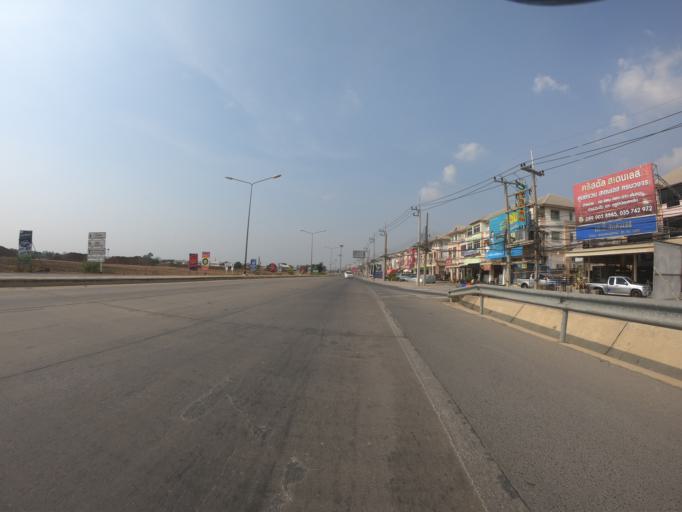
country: TH
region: Phra Nakhon Si Ayutthaya
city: Phra Nakhon Si Ayutthaya
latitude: 14.3336
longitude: 100.6060
